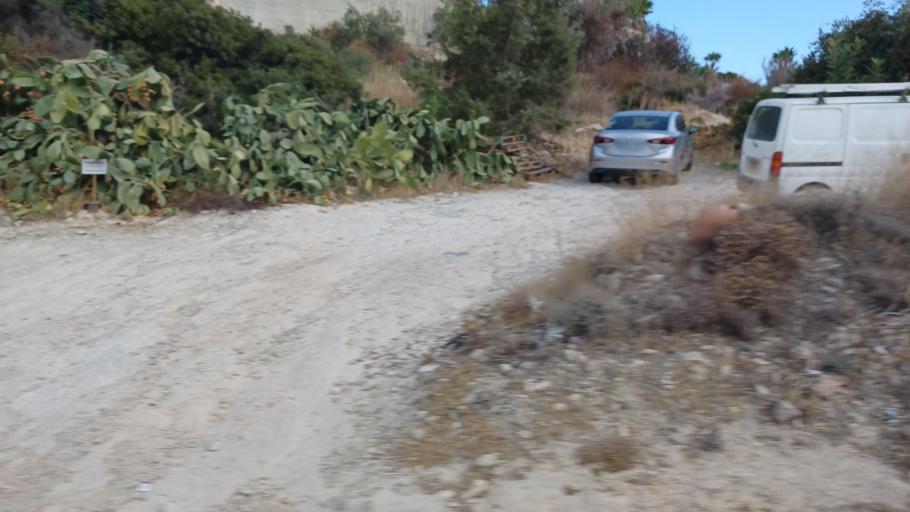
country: CY
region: Limassol
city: Pano Polemidia
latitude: 34.7209
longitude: 33.0171
